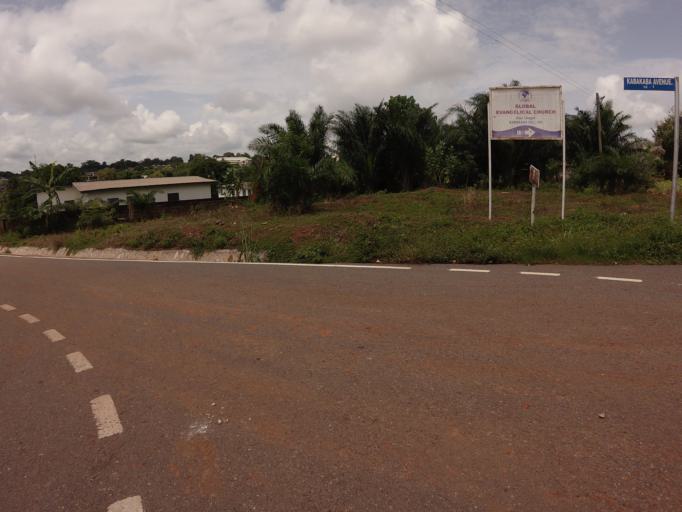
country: GH
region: Volta
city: Ho
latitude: 6.6120
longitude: 0.4565
